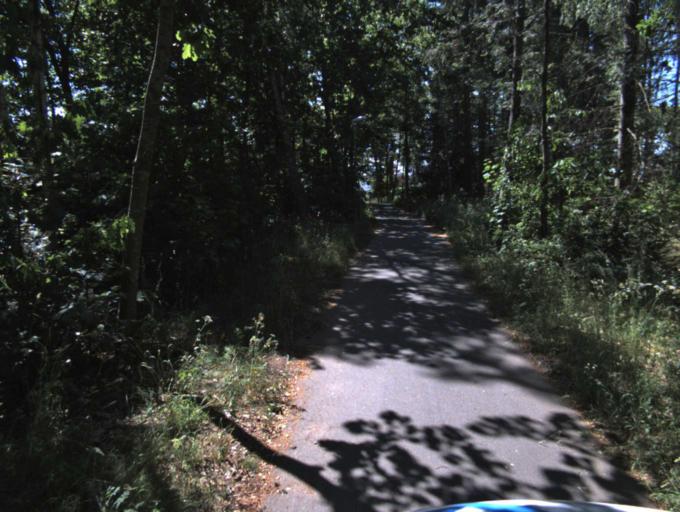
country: SE
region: Skane
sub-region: Kristianstads Kommun
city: Onnestad
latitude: 56.0680
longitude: 14.0876
